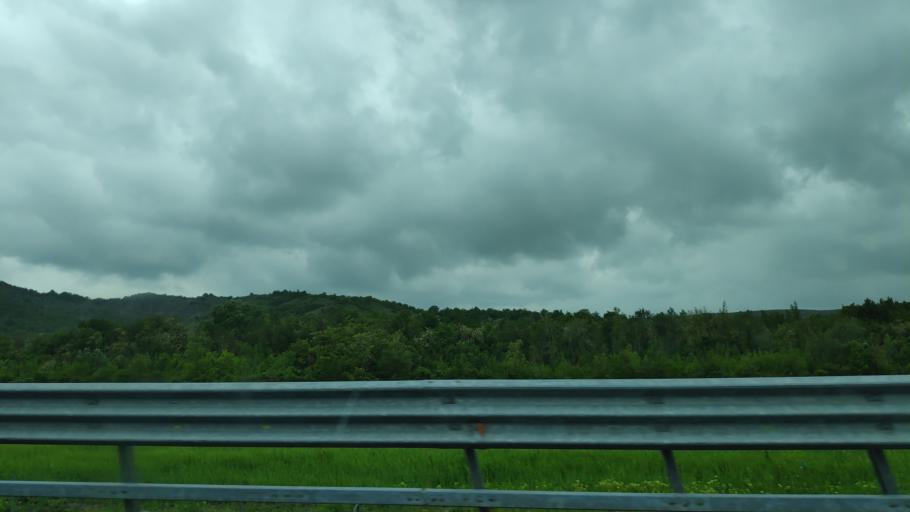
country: IT
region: Emilia-Romagna
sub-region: Provincia di Parma
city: Ramiola
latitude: 44.6669
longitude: 10.0591
